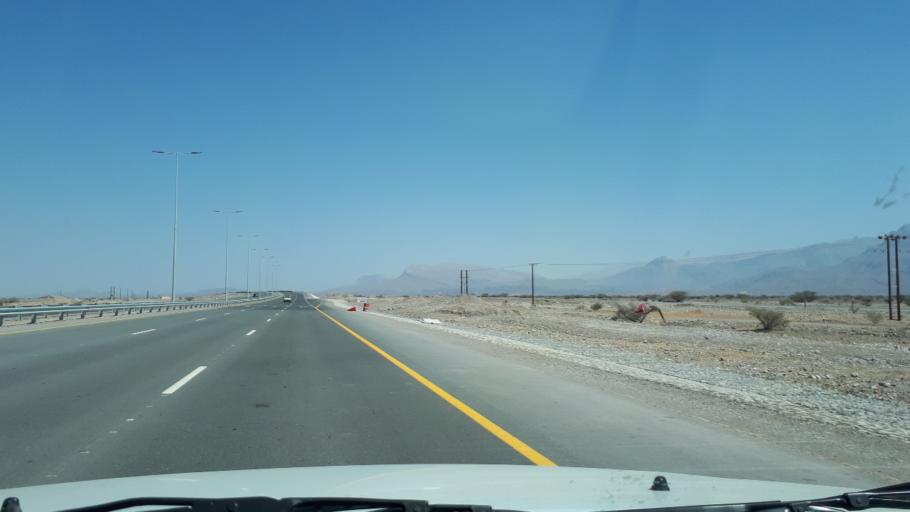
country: OM
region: Ash Sharqiyah
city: Badiyah
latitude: 22.3526
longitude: 59.1163
